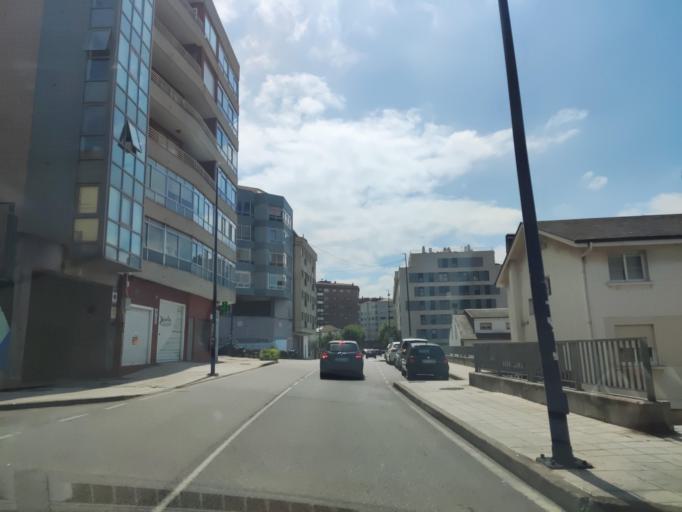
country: ES
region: Galicia
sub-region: Provincia de Pontevedra
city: Vigo
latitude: 42.2505
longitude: -8.6984
